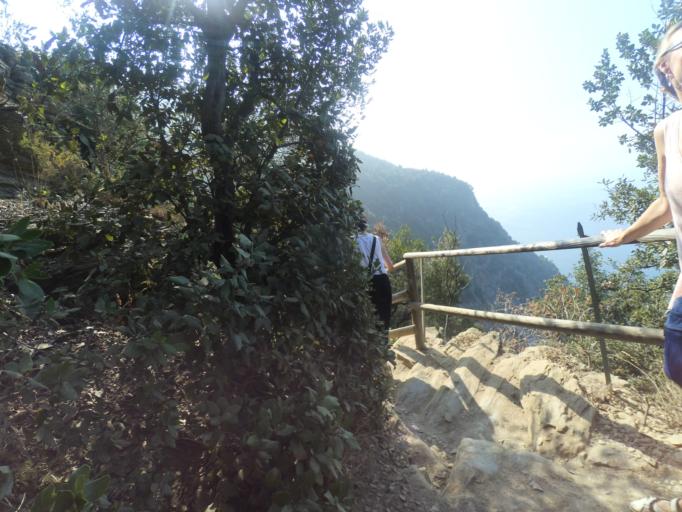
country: IT
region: Liguria
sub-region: Provincia di La Spezia
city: Vernazza
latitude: 44.1405
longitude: 9.6752
